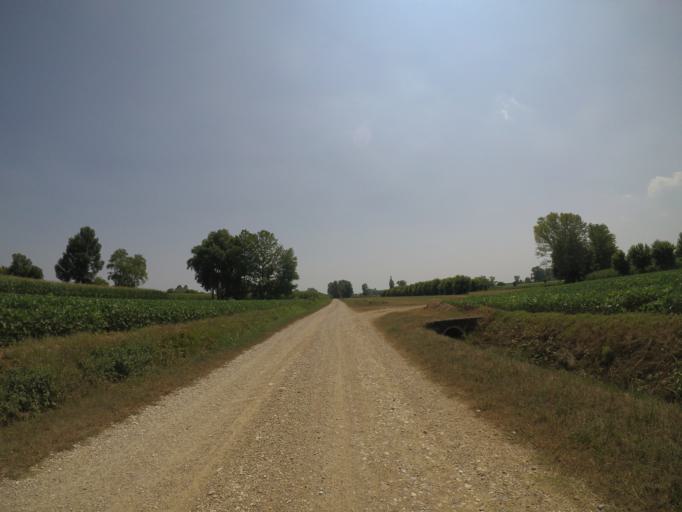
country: IT
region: Friuli Venezia Giulia
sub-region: Provincia di Udine
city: Talmassons
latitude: 45.9213
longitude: 13.1234
